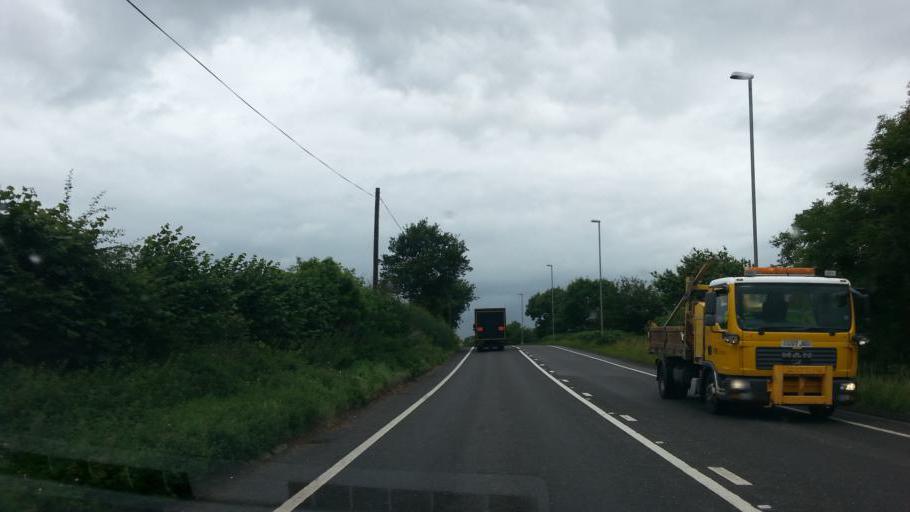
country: GB
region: England
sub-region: Nottinghamshire
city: Bilsthorpe
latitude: 53.1327
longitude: -1.0525
